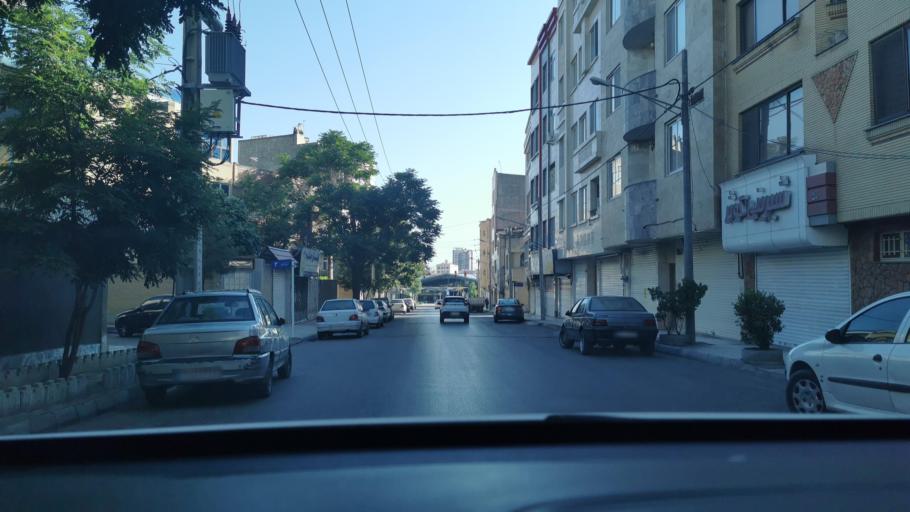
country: IR
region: Razavi Khorasan
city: Mashhad
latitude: 36.3087
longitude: 59.5111
